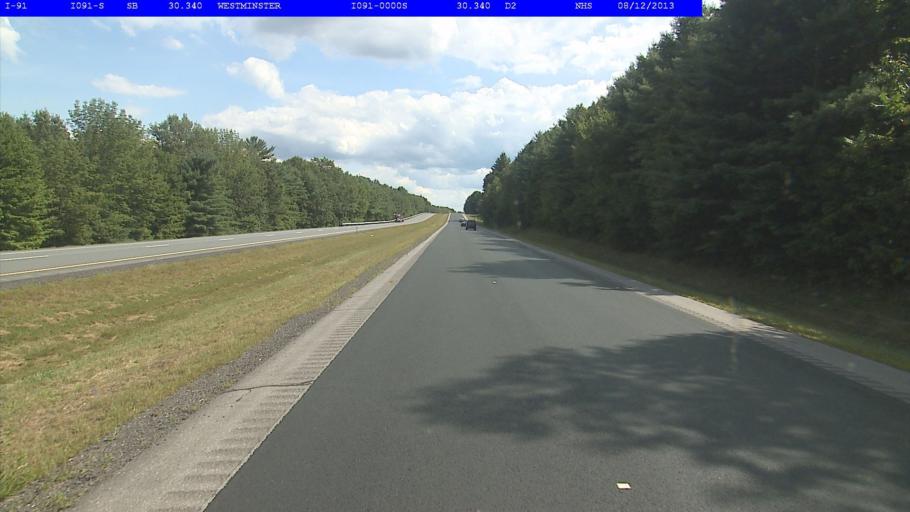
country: US
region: Vermont
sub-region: Windham County
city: Bellows Falls
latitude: 43.1152
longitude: -72.4600
